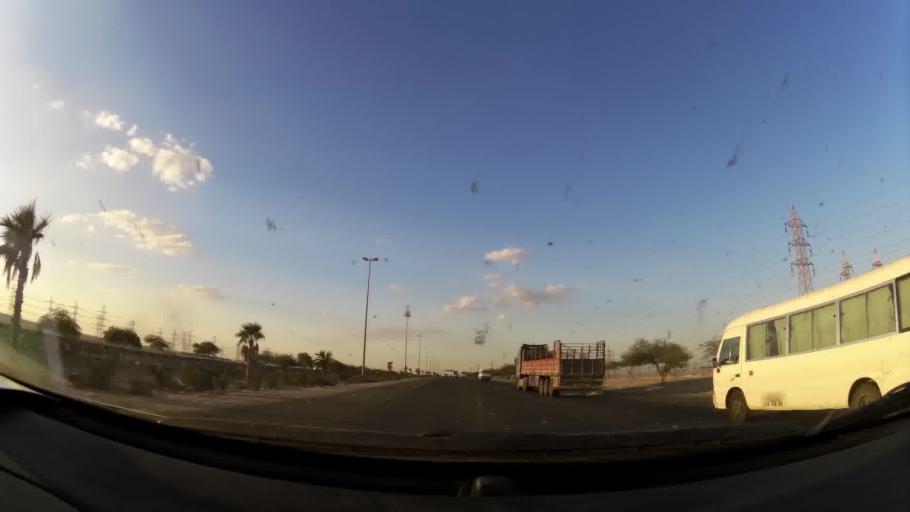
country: KW
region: Al Ahmadi
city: Al Fahahil
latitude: 28.8738
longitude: 48.2327
